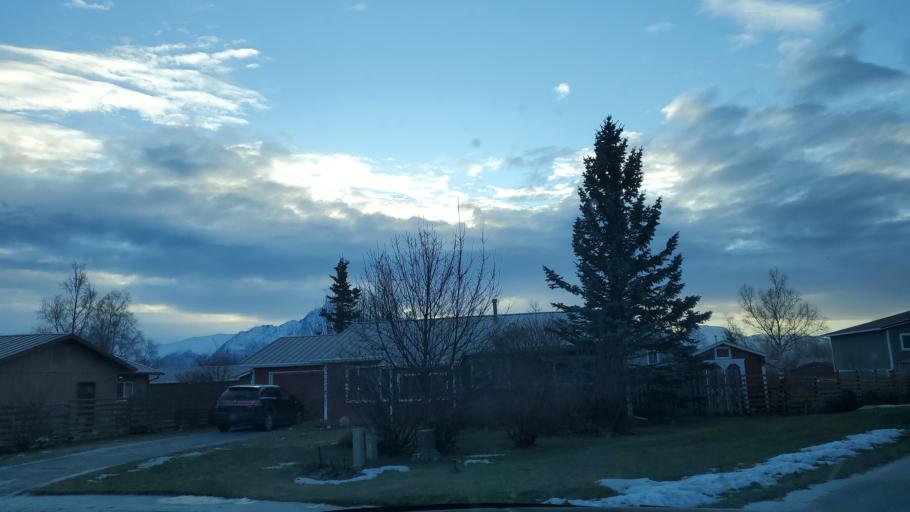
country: US
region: Alaska
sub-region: Matanuska-Susitna Borough
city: Palmer
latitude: 61.6156
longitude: -149.1049
